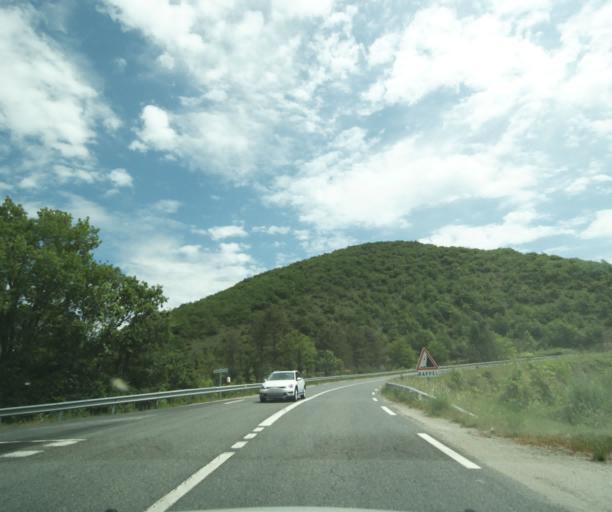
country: FR
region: Midi-Pyrenees
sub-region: Departement de l'Aveyron
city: Saint-Affrique
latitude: 43.9567
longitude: 2.9479
